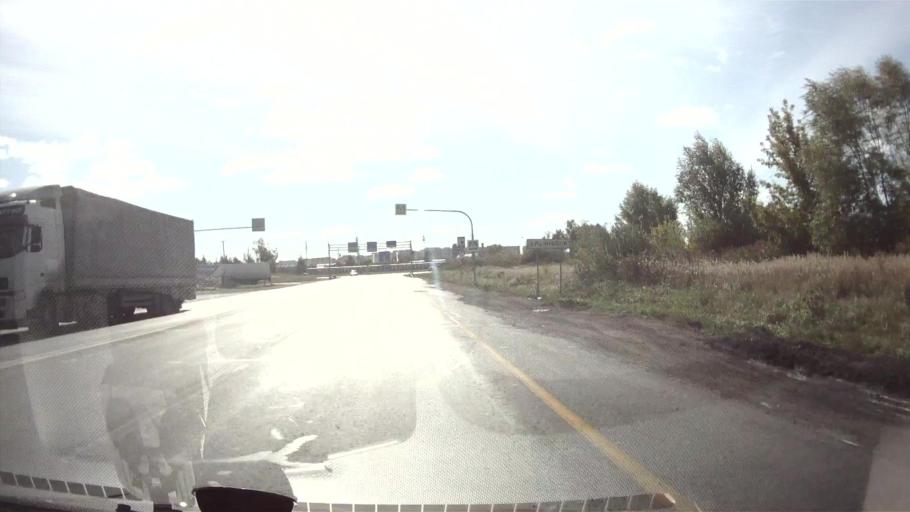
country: RU
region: Ulyanovsk
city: Isheyevka
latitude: 54.2934
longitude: 48.2520
